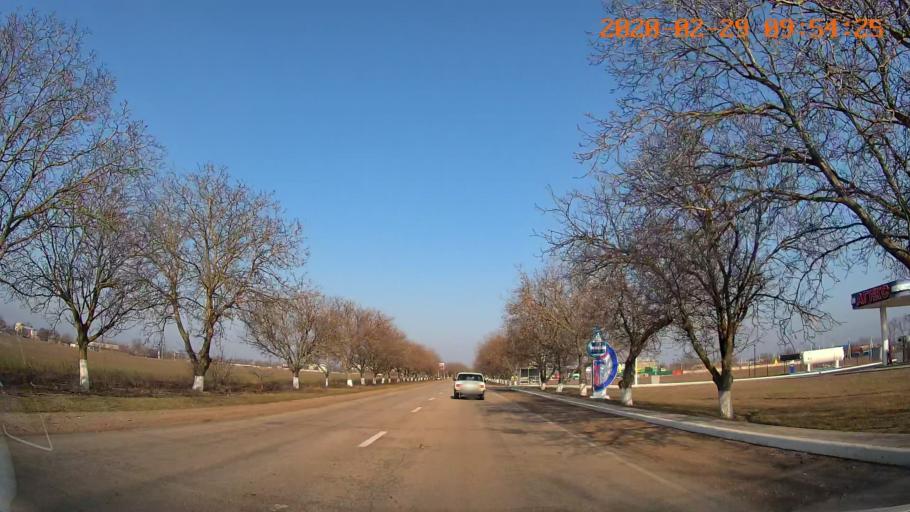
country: MD
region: Telenesti
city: Slobozia
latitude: 46.7284
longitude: 29.7160
